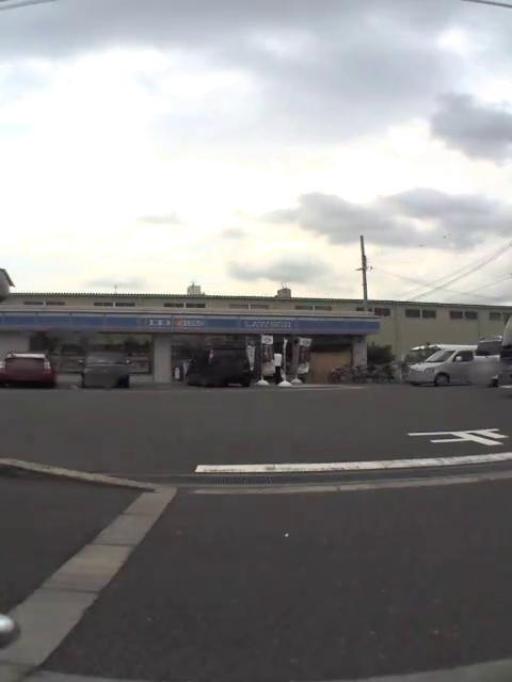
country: JP
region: Osaka
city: Neyagawa
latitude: 34.7564
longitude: 135.6265
